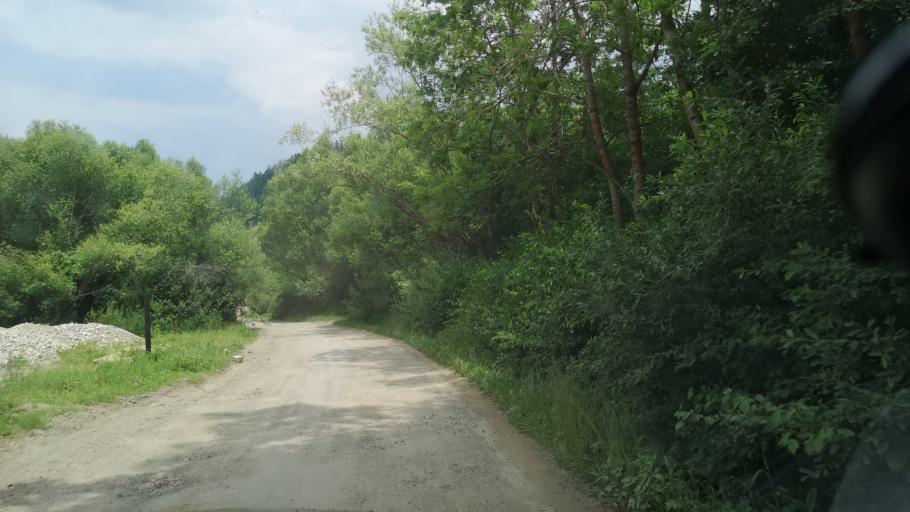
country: SK
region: Zilinsky
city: Ruzomberok
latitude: 49.1311
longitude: 19.4192
